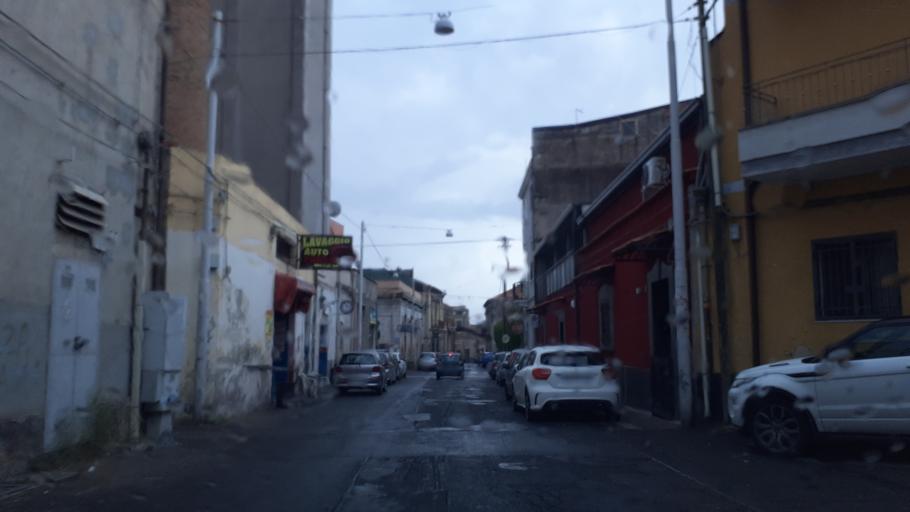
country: IT
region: Sicily
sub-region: Catania
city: Catania
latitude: 37.5043
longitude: 15.0713
